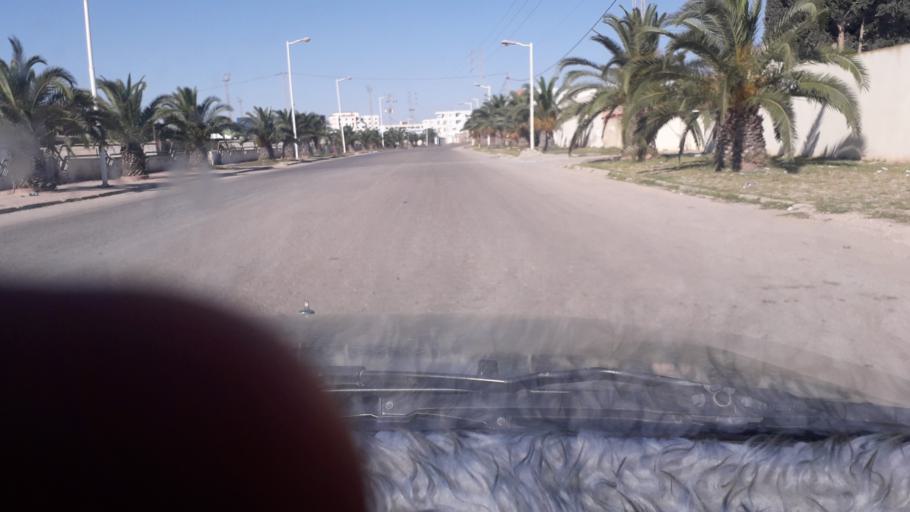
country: TN
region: Safaqis
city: Al Qarmadah
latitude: 34.8453
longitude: 10.7612
